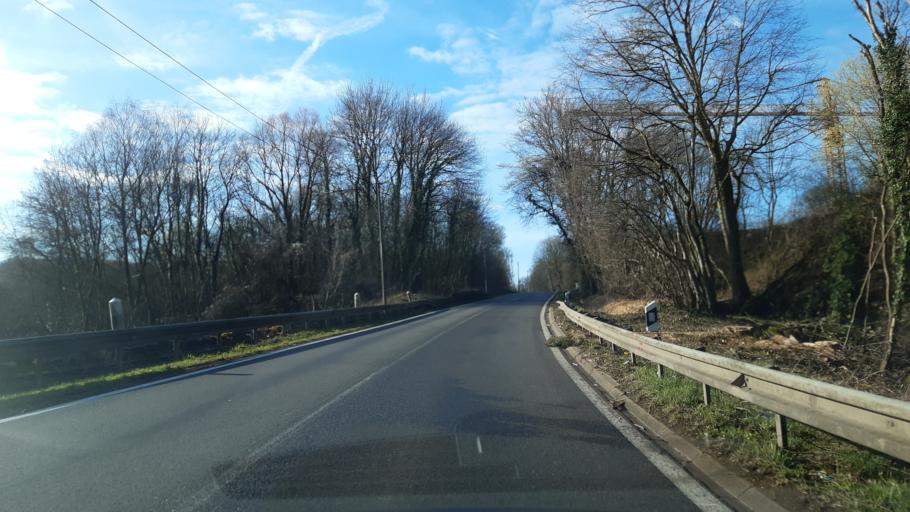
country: FR
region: Lorraine
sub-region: Departement de la Moselle
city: Audun-le-Tiche
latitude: 49.4629
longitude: 5.9642
